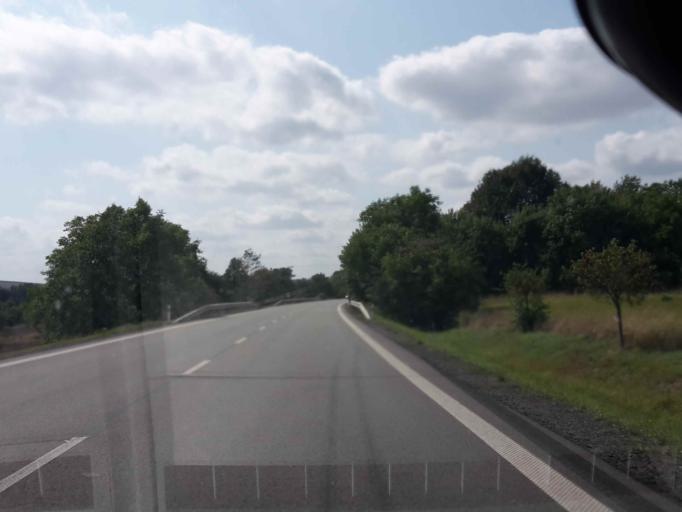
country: CZ
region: South Moravian
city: Rousinov
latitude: 49.2120
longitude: 16.8982
